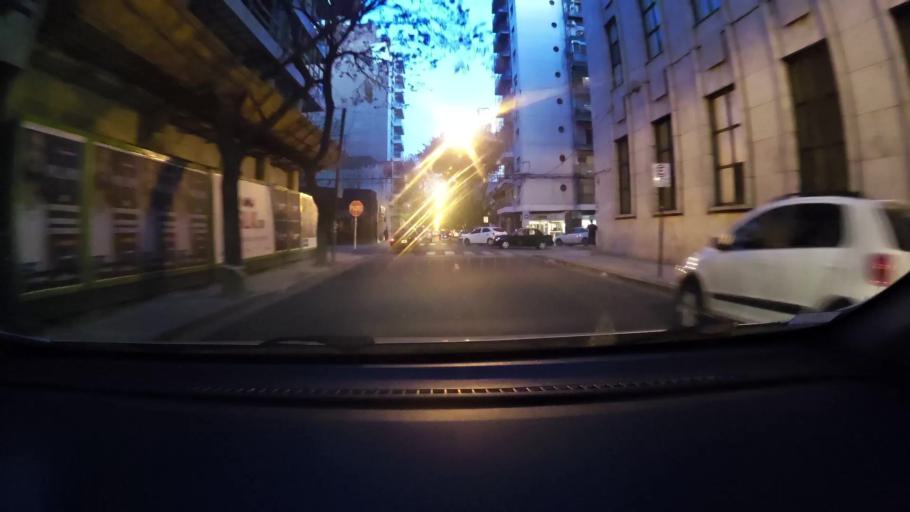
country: AR
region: Santa Fe
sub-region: Departamento de Rosario
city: Rosario
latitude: -32.9539
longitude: -60.6534
